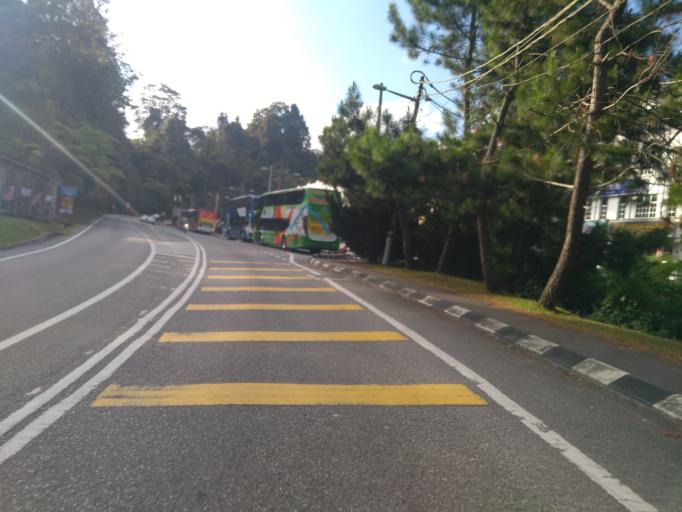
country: MY
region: Pahang
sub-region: Cameron Highlands
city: Tanah Rata
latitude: 4.4724
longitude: 101.3805
